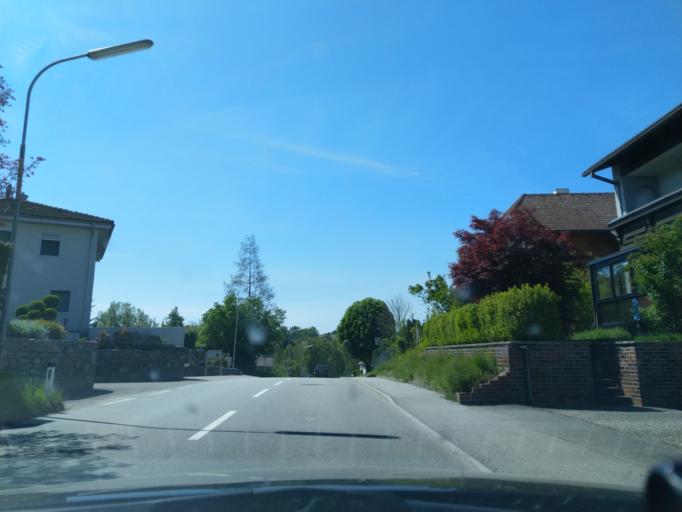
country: AT
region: Upper Austria
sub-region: Politischer Bezirk Ried im Innkreis
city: Ried im Innkreis
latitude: 48.2488
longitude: 13.4520
